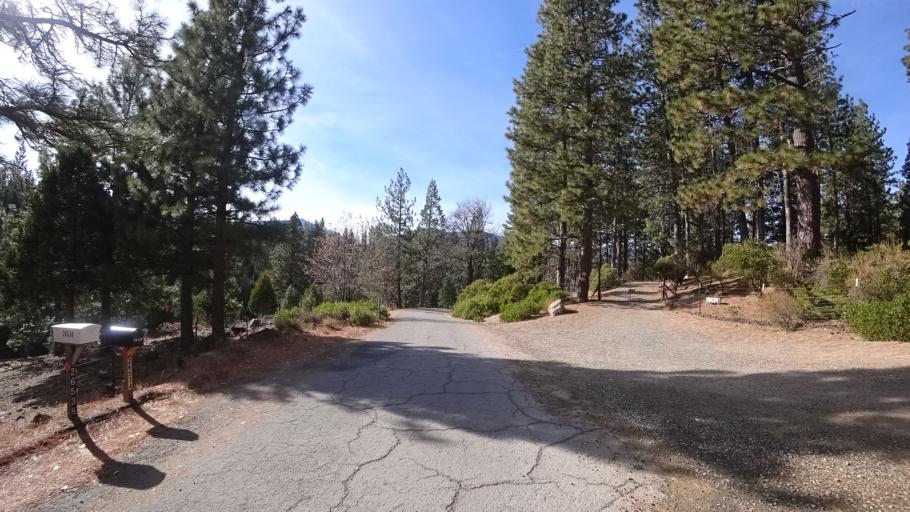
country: US
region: California
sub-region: Siskiyou County
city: Weed
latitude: 41.4334
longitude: -122.4206
